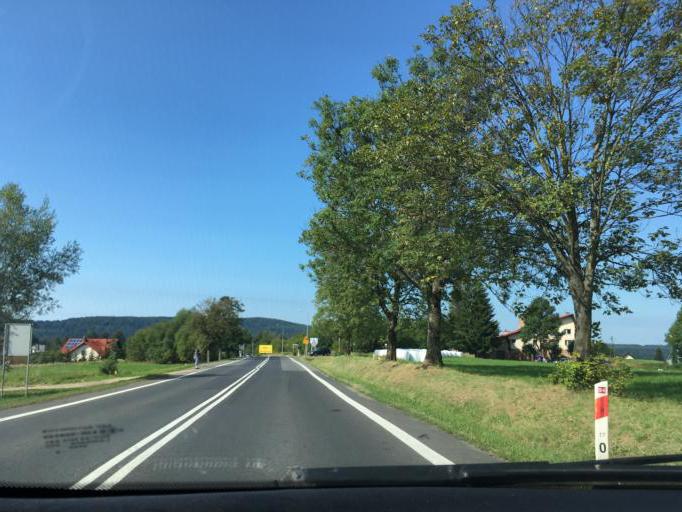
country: PL
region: Subcarpathian Voivodeship
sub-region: Powiat leski
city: Lesko
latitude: 49.4667
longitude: 22.3454
